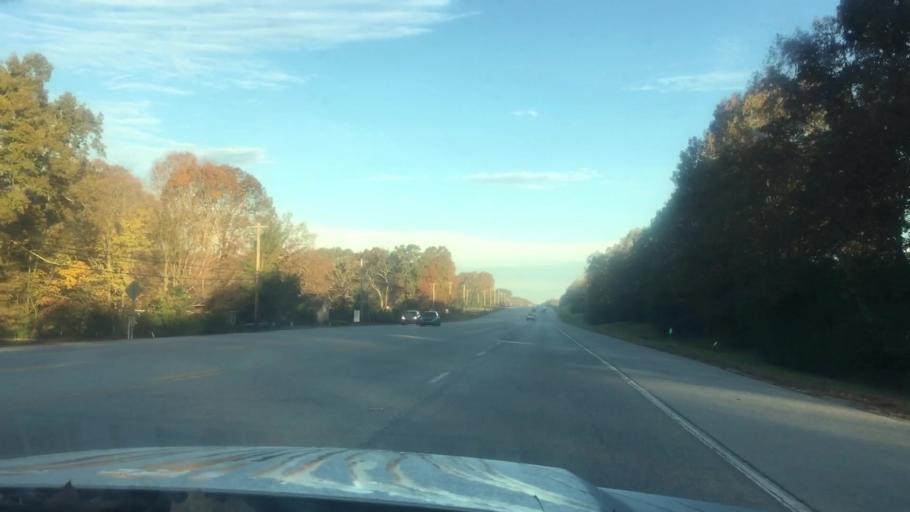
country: US
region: Tennessee
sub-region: Coffee County
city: Tullahoma
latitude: 35.3216
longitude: -86.1731
